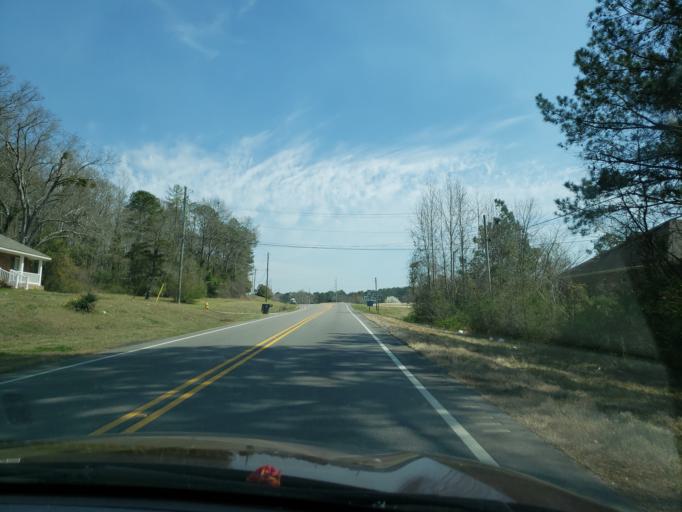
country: US
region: Alabama
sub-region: Elmore County
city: Wetumpka
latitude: 32.5520
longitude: -86.1809
